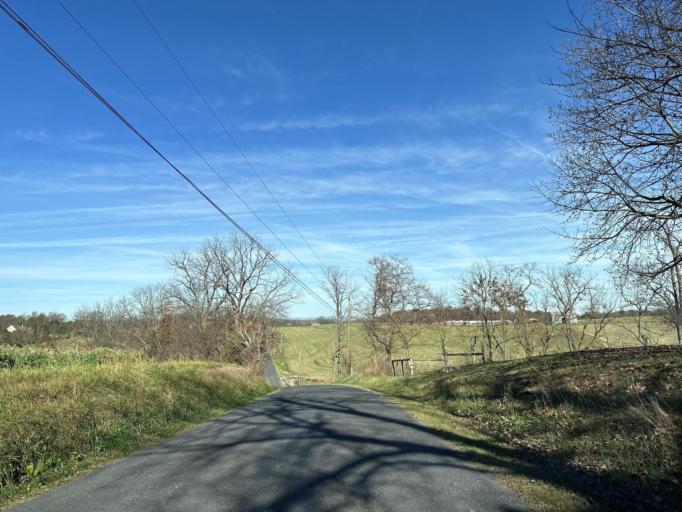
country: US
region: Virginia
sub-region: Augusta County
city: Weyers Cave
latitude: 38.2493
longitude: -78.9205
